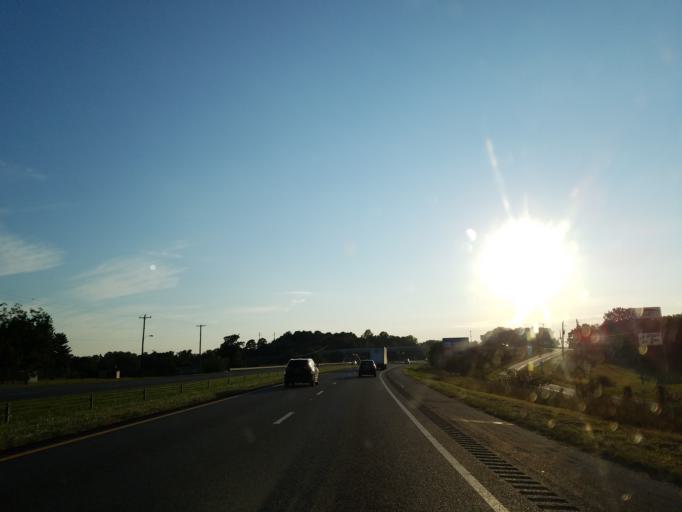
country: US
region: South Carolina
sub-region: Cherokee County
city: Gaffney
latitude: 35.0974
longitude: -81.6541
